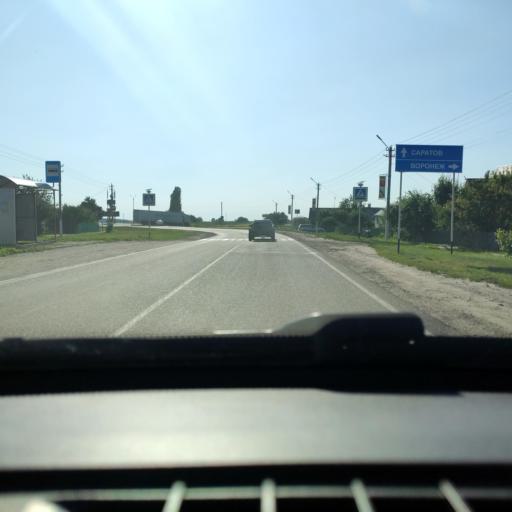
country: RU
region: Voronezj
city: Panino
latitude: 51.6447
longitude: 40.1200
